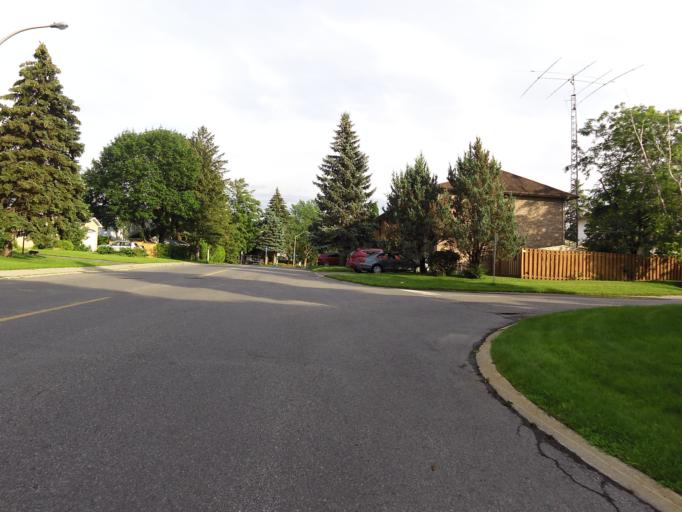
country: CA
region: Ontario
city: Bells Corners
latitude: 45.3298
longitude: -75.7932
